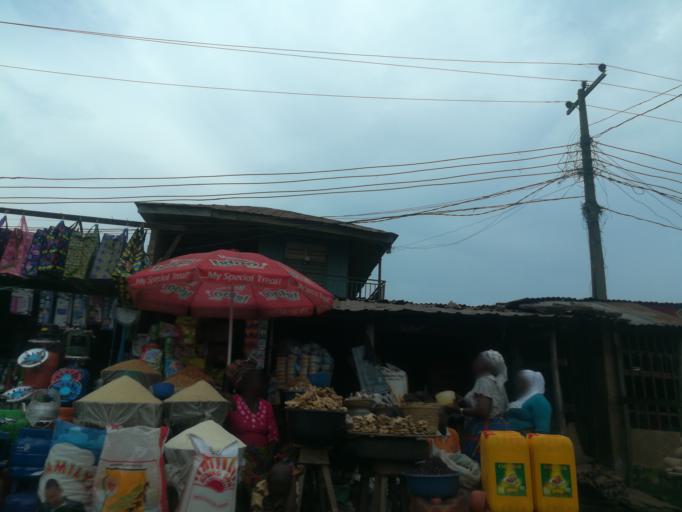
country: NG
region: Oyo
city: Ibadan
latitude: 7.4339
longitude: 3.9129
